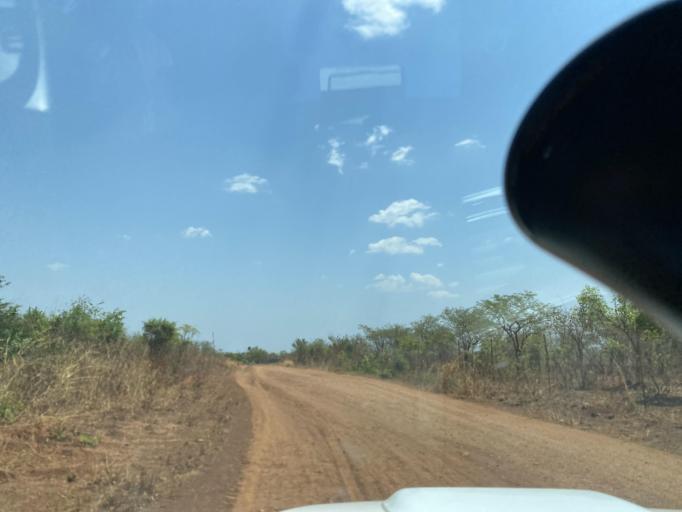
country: ZM
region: Lusaka
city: Lusaka
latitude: -15.5059
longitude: 28.0205
